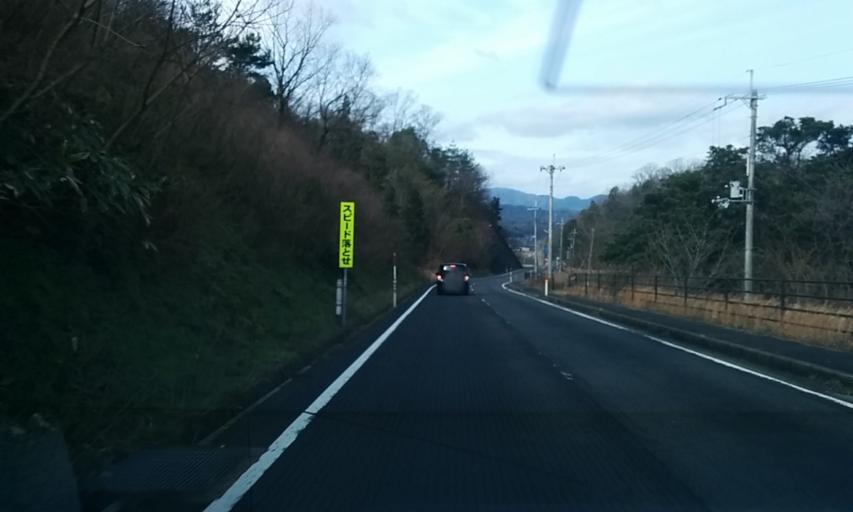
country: JP
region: Kyoto
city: Miyazu
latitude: 35.5830
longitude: 135.1117
